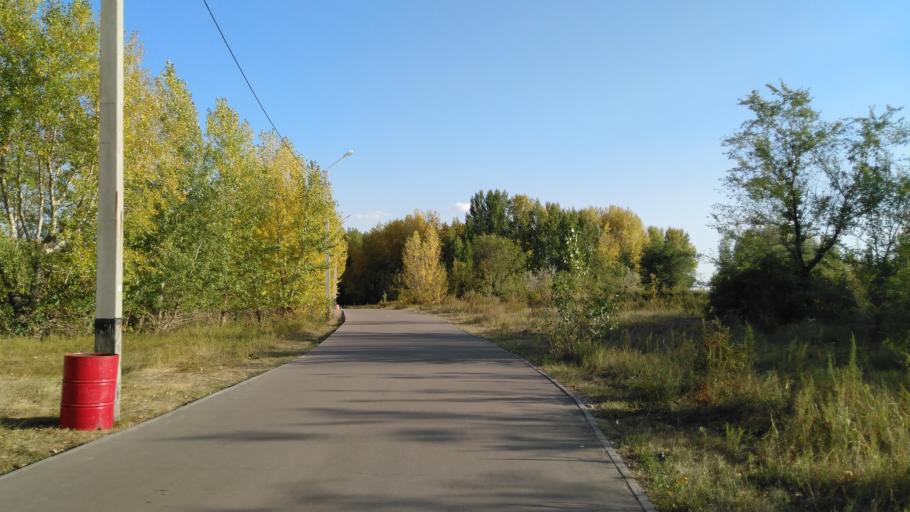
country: KZ
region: Pavlodar
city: Pavlodar
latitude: 52.2616
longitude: 76.9331
